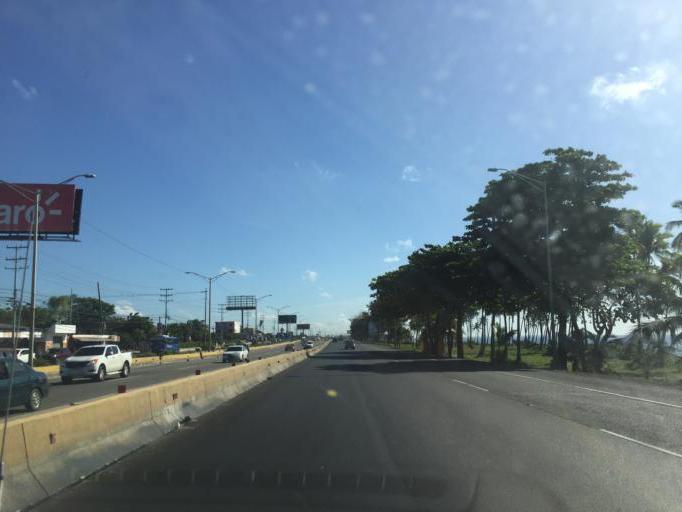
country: DO
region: Santo Domingo
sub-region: Santo Domingo
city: Santo Domingo Este
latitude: 18.4662
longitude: -69.7892
